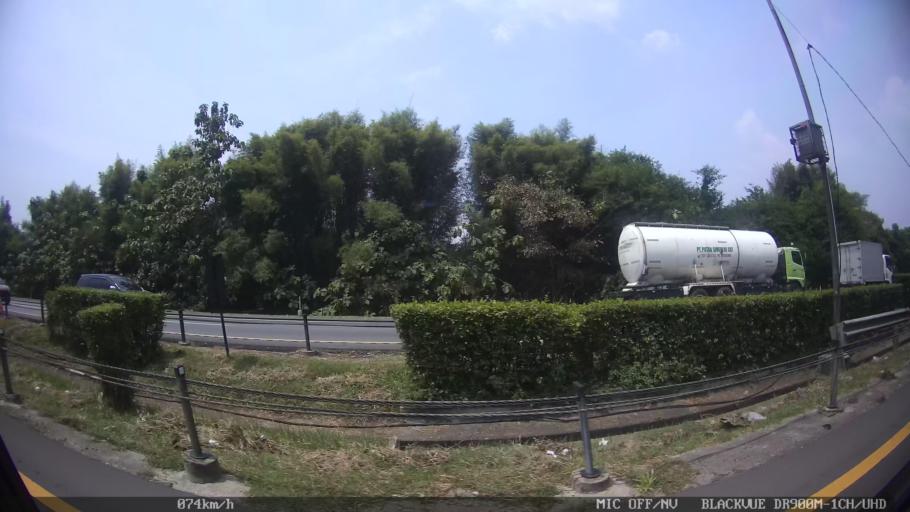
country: ID
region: Banten
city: Serang
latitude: -6.0854
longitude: 106.1372
